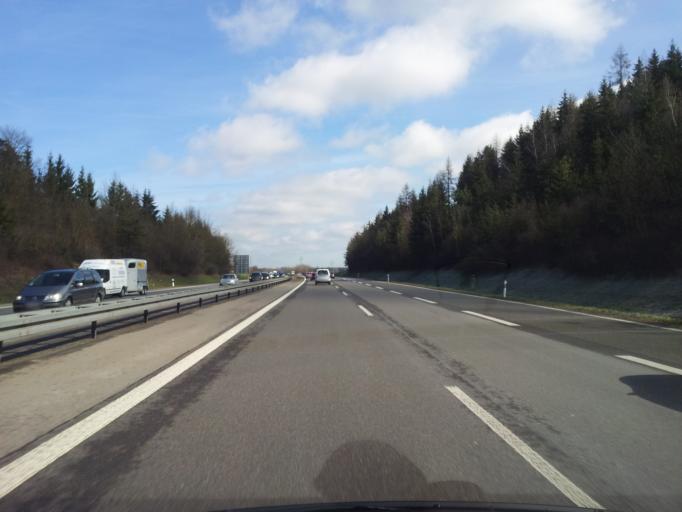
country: DE
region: Baden-Wuerttemberg
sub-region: Freiburg Region
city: Tuningen
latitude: 48.0355
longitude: 8.6210
